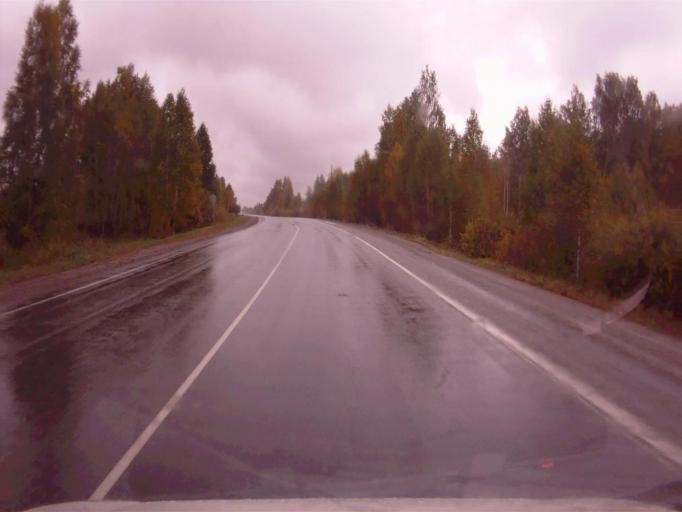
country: RU
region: Chelyabinsk
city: Argayash
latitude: 55.4865
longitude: 60.7355
